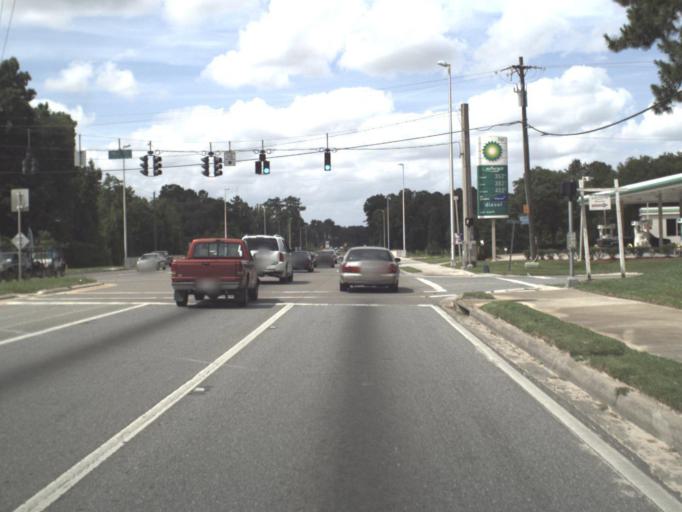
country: US
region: Florida
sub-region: Clay County
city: Middleburg
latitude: 30.0734
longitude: -81.8644
